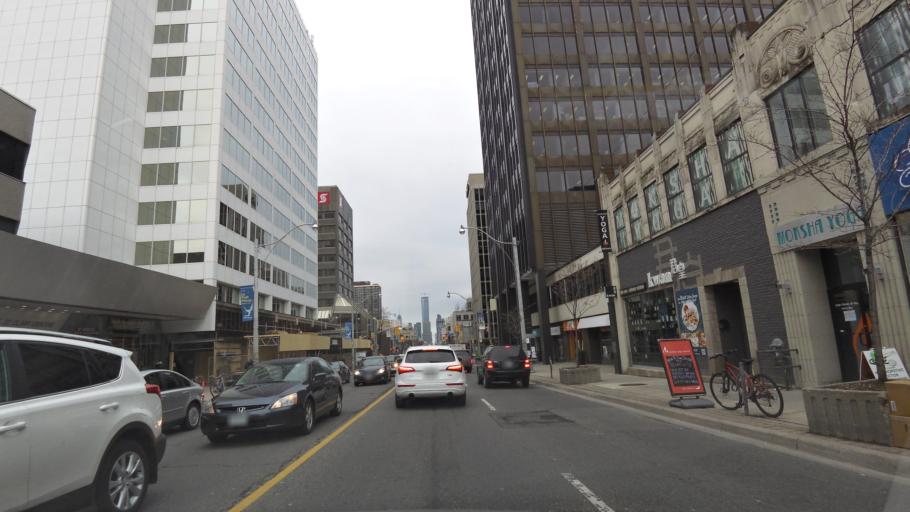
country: CA
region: Ontario
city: Toronto
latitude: 43.6888
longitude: -79.3943
